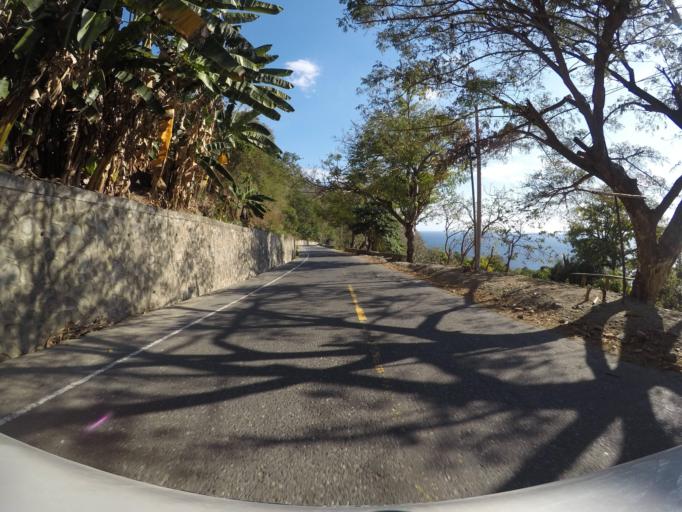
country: TL
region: Liquica
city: Maubara
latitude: -8.6625
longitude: 125.1143
